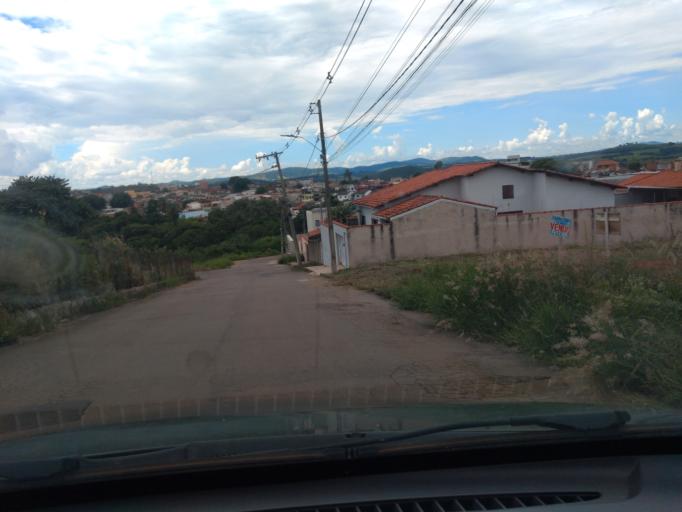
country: BR
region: Minas Gerais
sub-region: Tres Coracoes
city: Tres Coracoes
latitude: -21.6878
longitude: -45.2657
